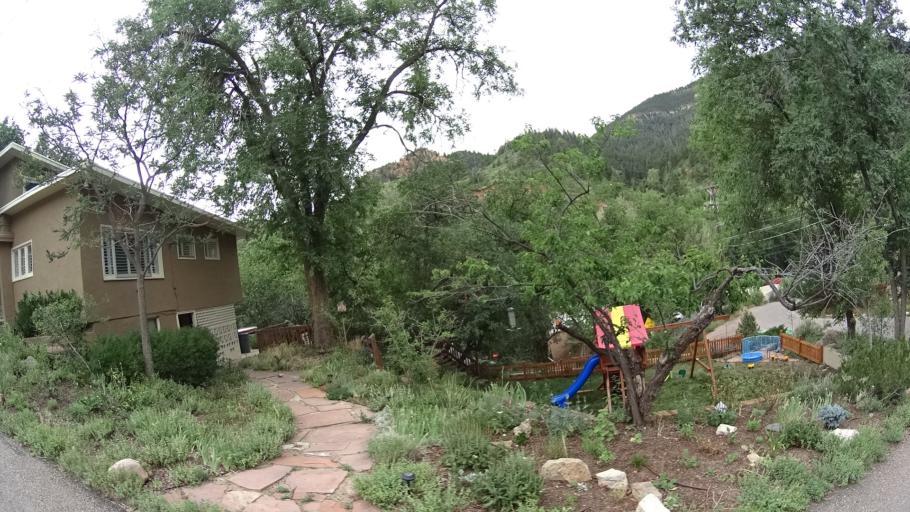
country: US
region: Colorado
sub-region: El Paso County
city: Manitou Springs
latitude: 38.8583
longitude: -104.9268
